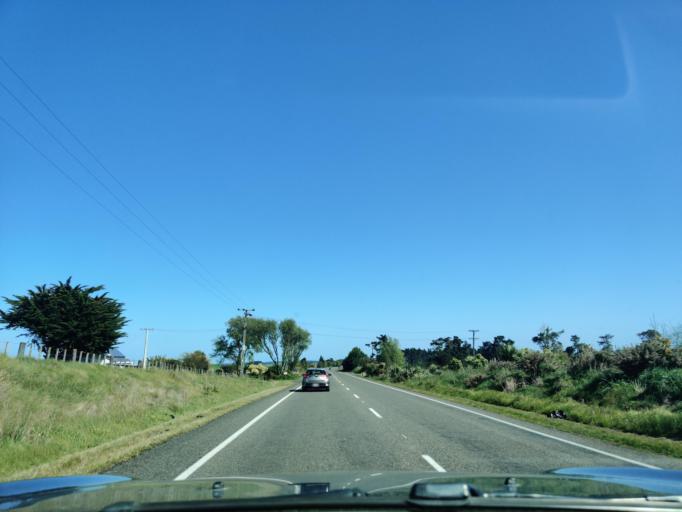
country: NZ
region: Manawatu-Wanganui
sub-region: Rangitikei District
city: Bulls
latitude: -40.0795
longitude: 175.2431
